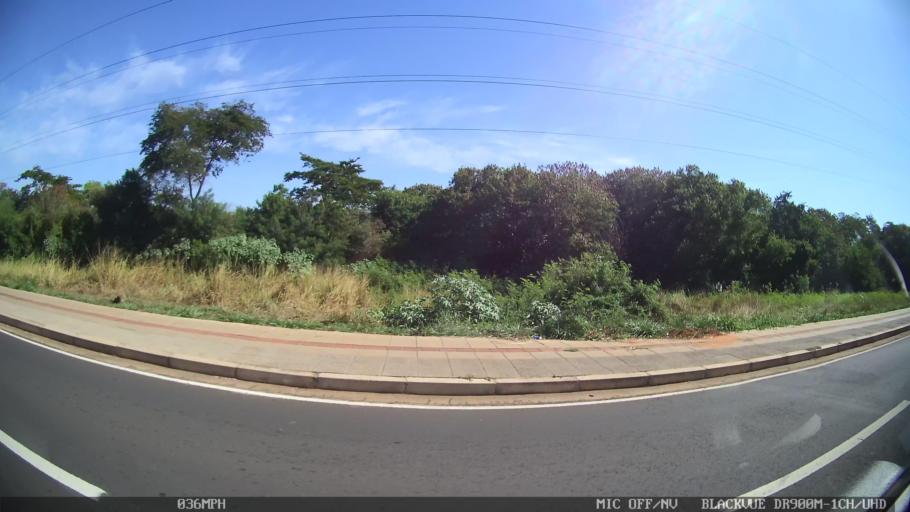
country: BR
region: Sao Paulo
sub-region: Sao Jose Do Rio Preto
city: Sao Jose do Rio Preto
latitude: -20.7792
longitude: -49.3822
